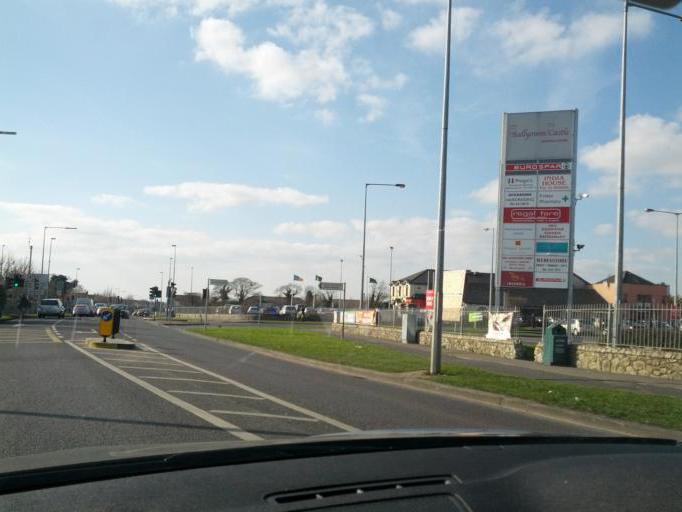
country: IE
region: Leinster
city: Lucan
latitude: 53.3466
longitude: -6.4227
